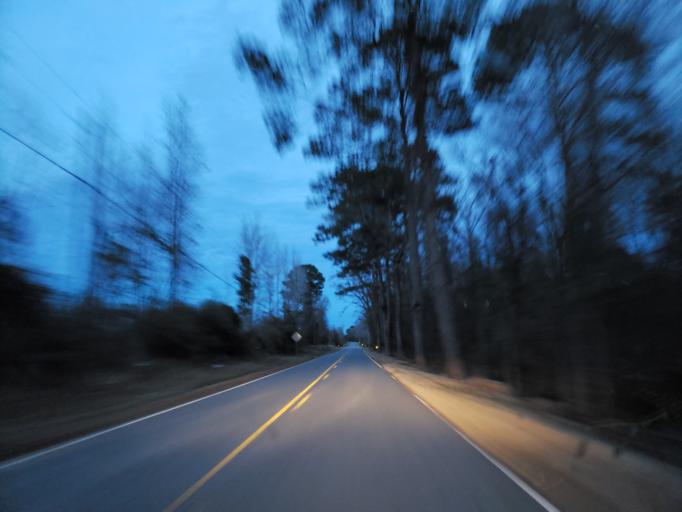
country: US
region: Alabama
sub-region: Greene County
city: Eutaw
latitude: 32.9068
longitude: -88.0111
